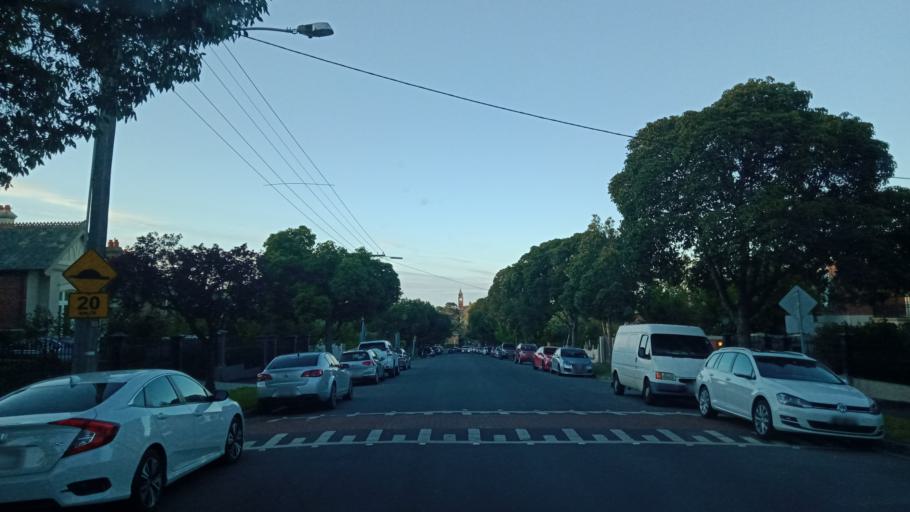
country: AU
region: Victoria
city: Glenferrie
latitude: -37.8322
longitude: 145.0413
